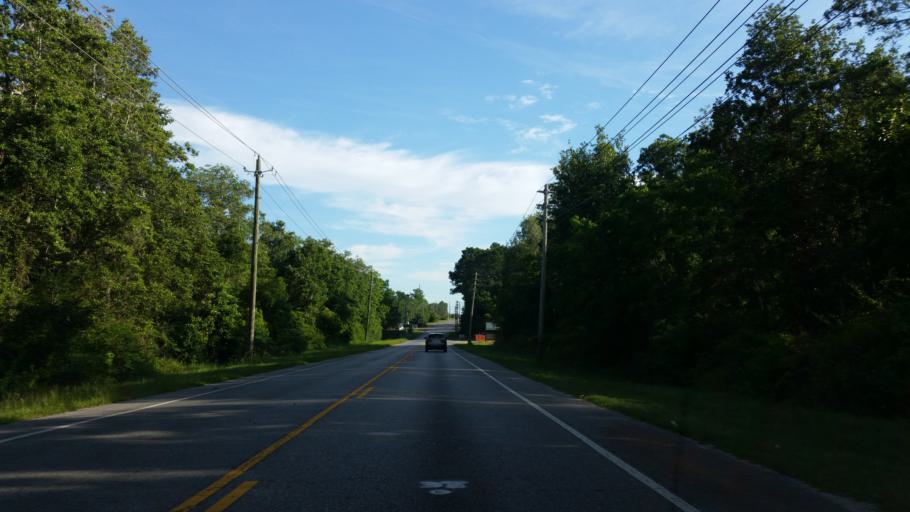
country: US
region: Florida
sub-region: Escambia County
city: Myrtle Grove
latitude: 30.4330
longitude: -87.3082
